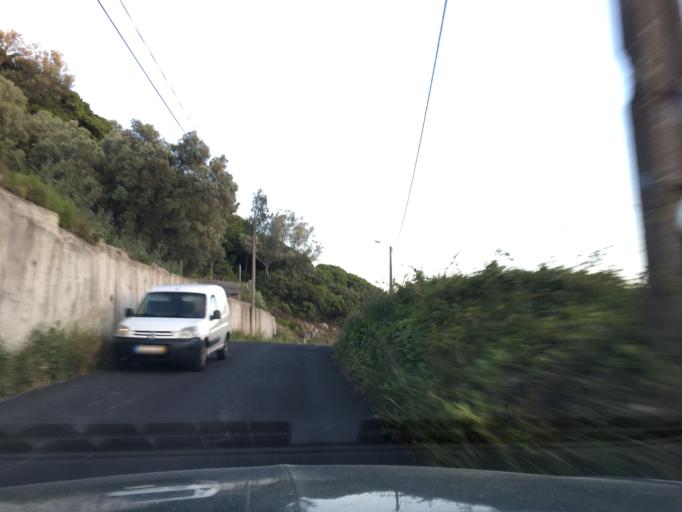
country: PT
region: Lisbon
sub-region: Oeiras
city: Quejas
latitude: 38.7191
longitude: -9.2760
